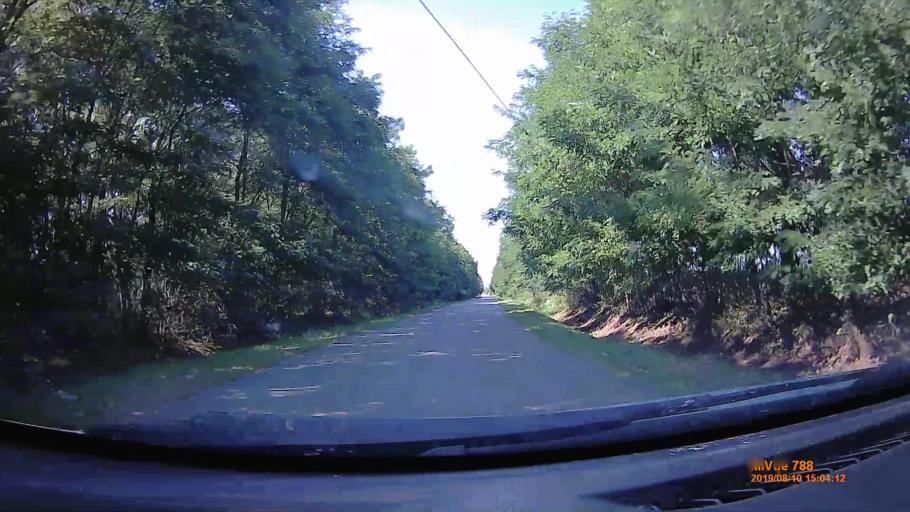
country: HU
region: Somogy
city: Lengyeltoti
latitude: 46.6729
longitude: 17.5672
